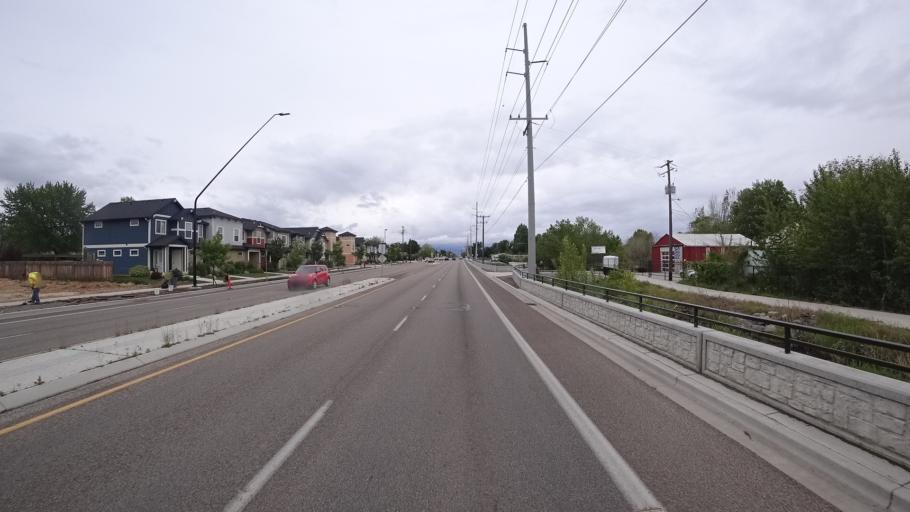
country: US
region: Idaho
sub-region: Ada County
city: Eagle
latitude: 43.6338
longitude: -116.3209
